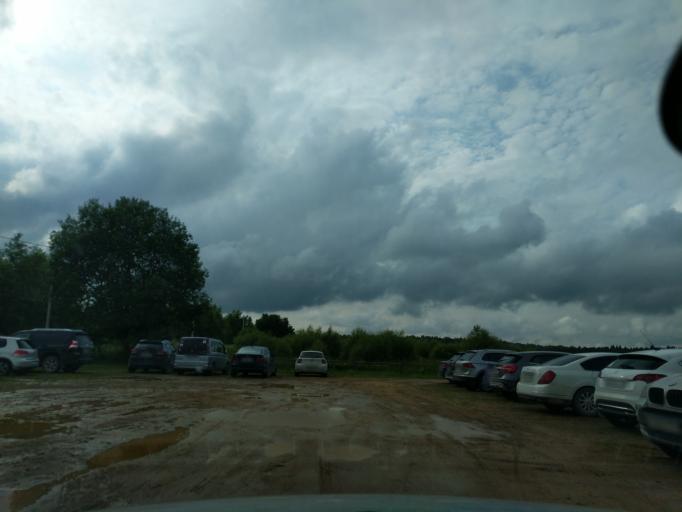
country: RU
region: Kaluga
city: Nikola-Lenivets
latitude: 54.7616
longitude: 35.5977
